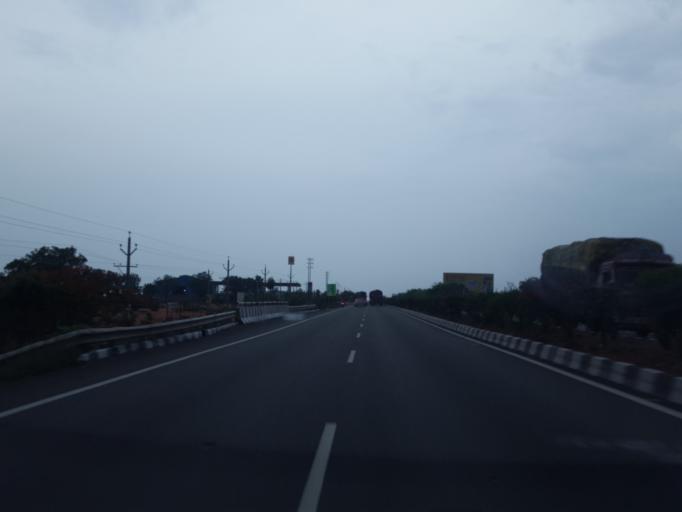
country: IN
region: Telangana
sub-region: Mahbubnagar
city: Farrukhnagar
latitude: 17.1054
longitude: 78.2565
